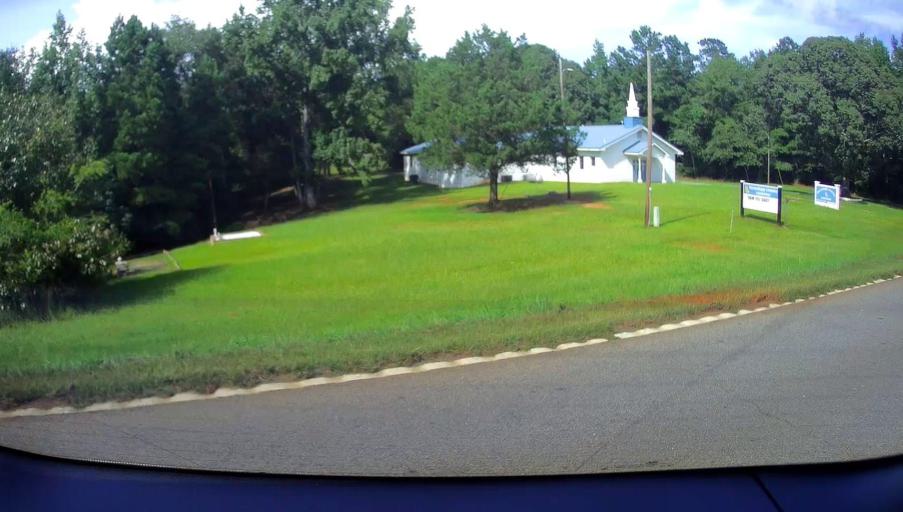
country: US
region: Georgia
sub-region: Upson County
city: Thomaston
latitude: 32.8769
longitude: -84.3579
